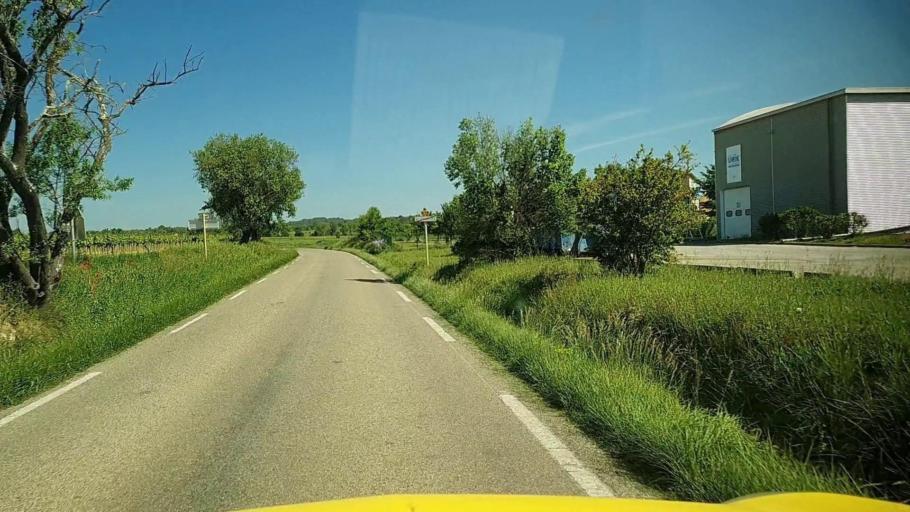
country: FR
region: Languedoc-Roussillon
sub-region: Departement du Gard
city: Saint-Chaptes
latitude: 43.9789
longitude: 4.2773
